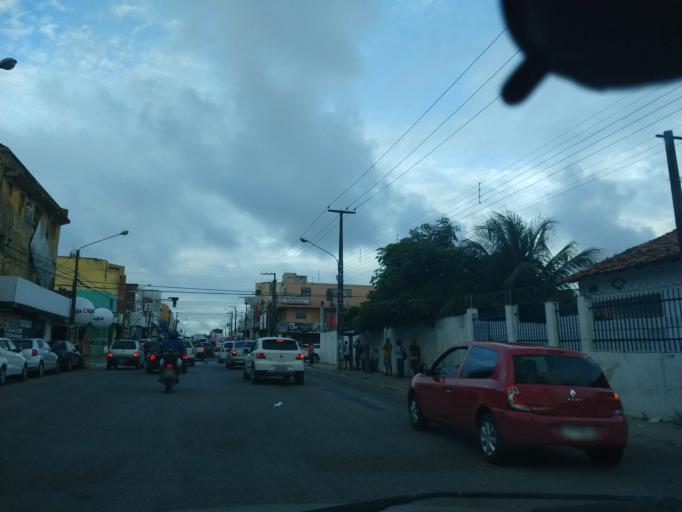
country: BR
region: Rio Grande do Norte
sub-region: Natal
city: Natal
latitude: -5.7985
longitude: -35.2198
